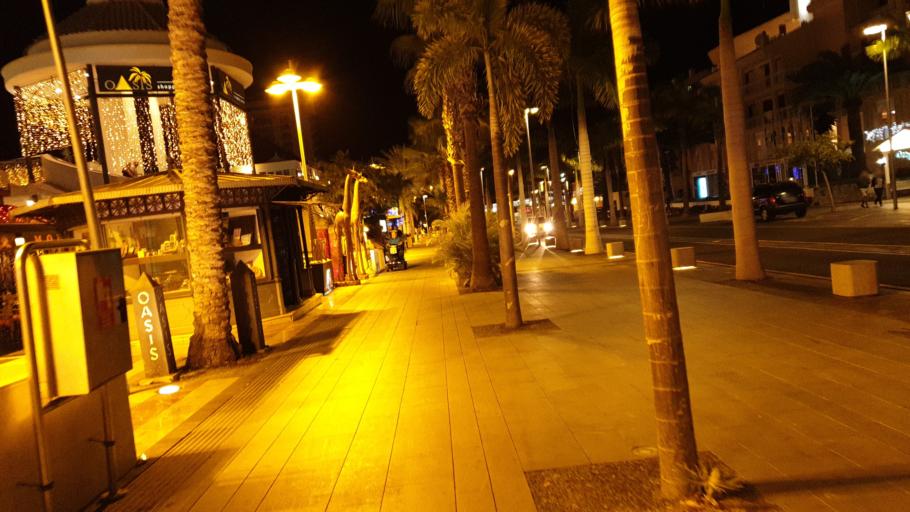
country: ES
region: Canary Islands
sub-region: Provincia de Santa Cruz de Tenerife
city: Playa de las Americas
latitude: 28.0544
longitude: -16.7283
